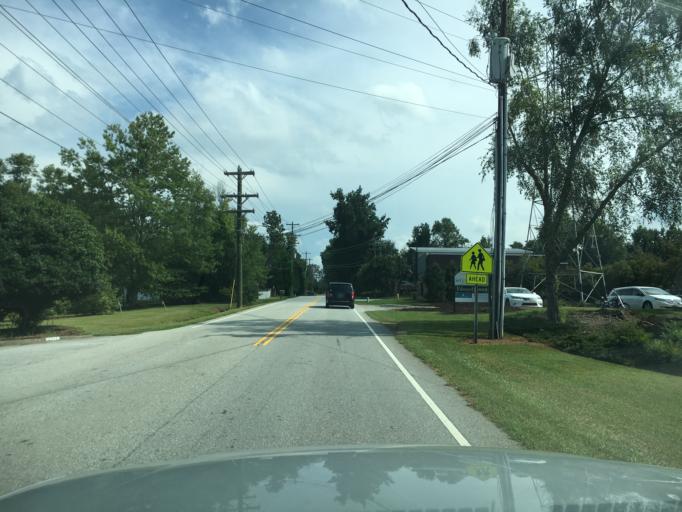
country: US
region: South Carolina
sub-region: Greenville County
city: Wade Hampton
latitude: 34.8513
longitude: -82.3172
